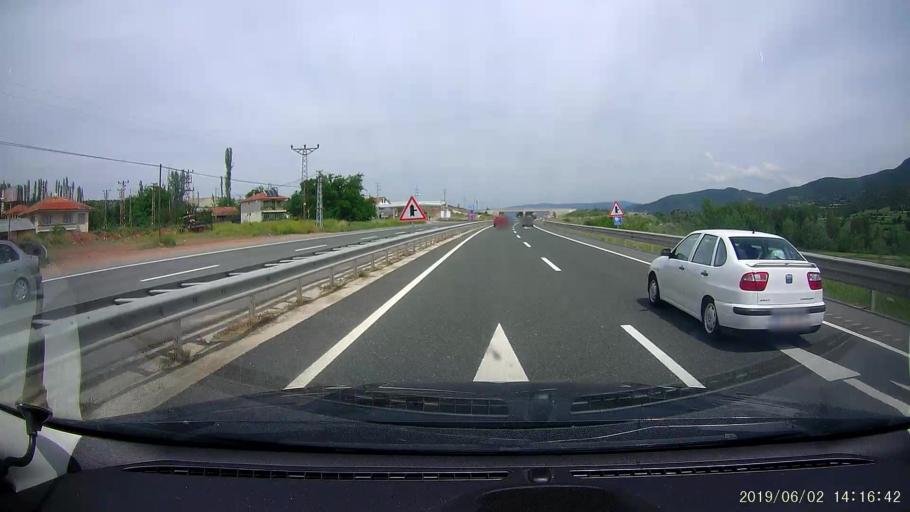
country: TR
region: Kastamonu
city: Tosya
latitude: 40.9506
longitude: 33.9151
